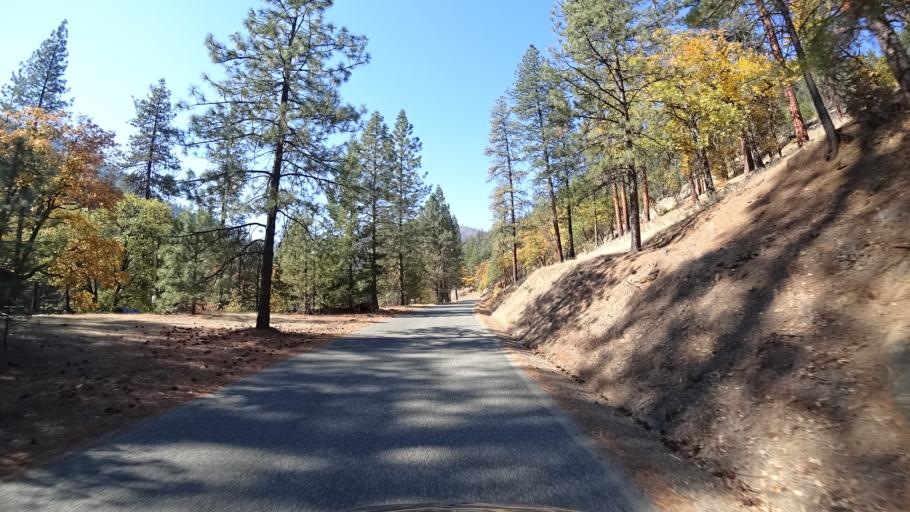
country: US
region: California
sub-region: Siskiyou County
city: Happy Camp
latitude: 41.6889
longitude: -123.0809
